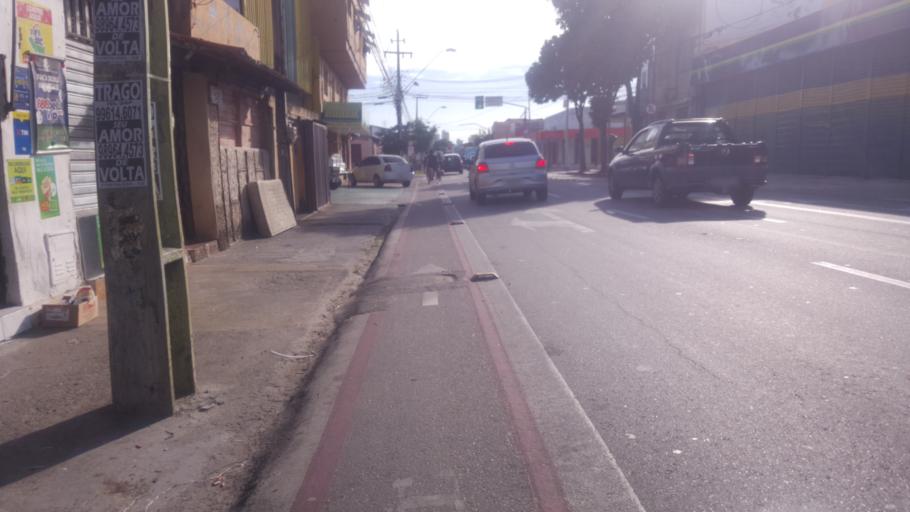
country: BR
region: Ceara
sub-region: Fortaleza
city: Fortaleza
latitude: -3.7576
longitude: -38.5426
